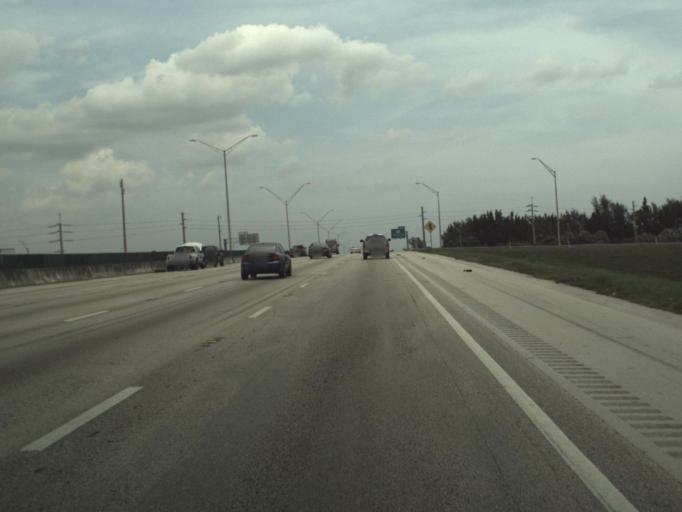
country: US
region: Florida
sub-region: Broward County
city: Kendall Green
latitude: 26.2586
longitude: -80.1346
